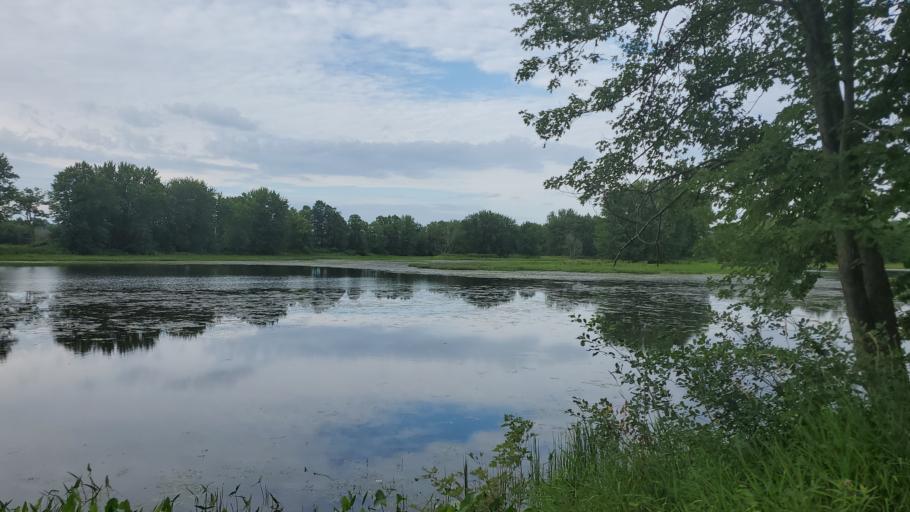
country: CA
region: Ontario
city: Clarence-Rockland
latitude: 45.5024
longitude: -75.4903
